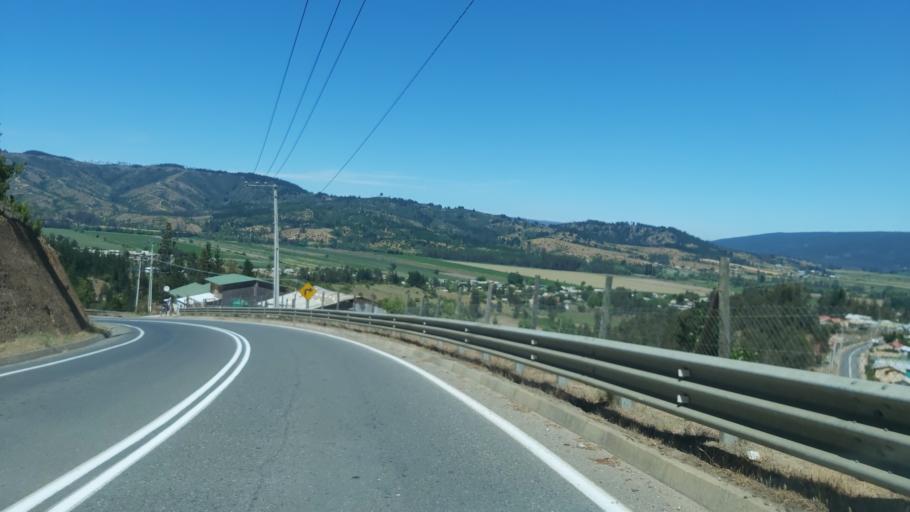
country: CL
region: Maule
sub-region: Provincia de Talca
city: Talca
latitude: -34.9840
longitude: -71.9736
